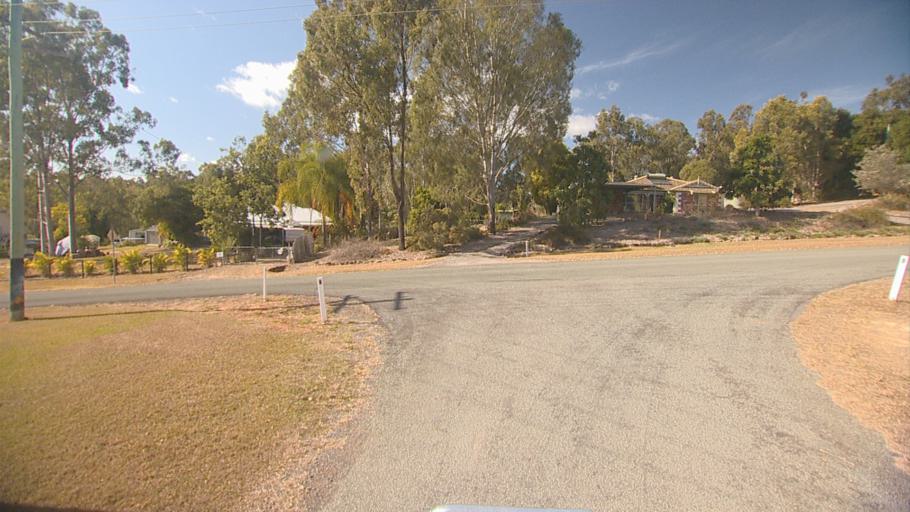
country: AU
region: Queensland
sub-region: Logan
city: Cedar Vale
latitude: -27.8544
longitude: 152.9854
